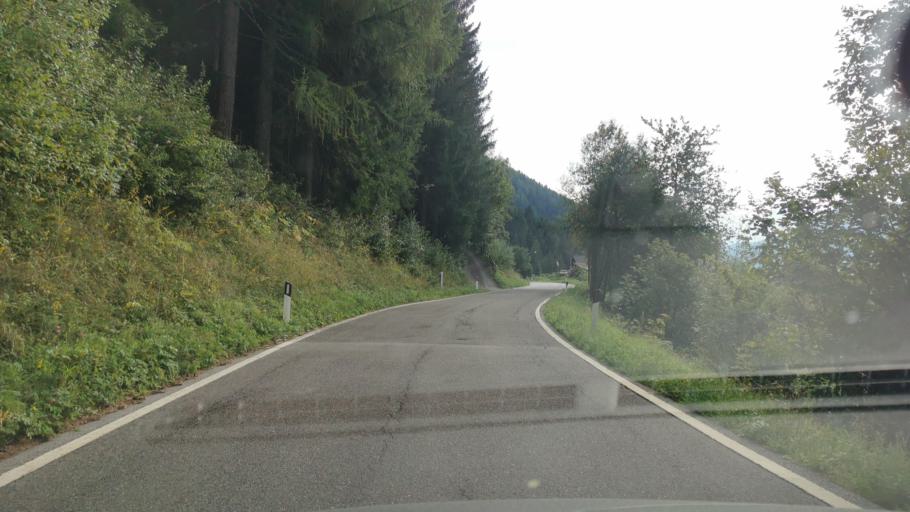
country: IT
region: Trentino-Alto Adige
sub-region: Provincia di Trento
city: Fierozzo
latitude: 46.1176
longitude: 11.3347
